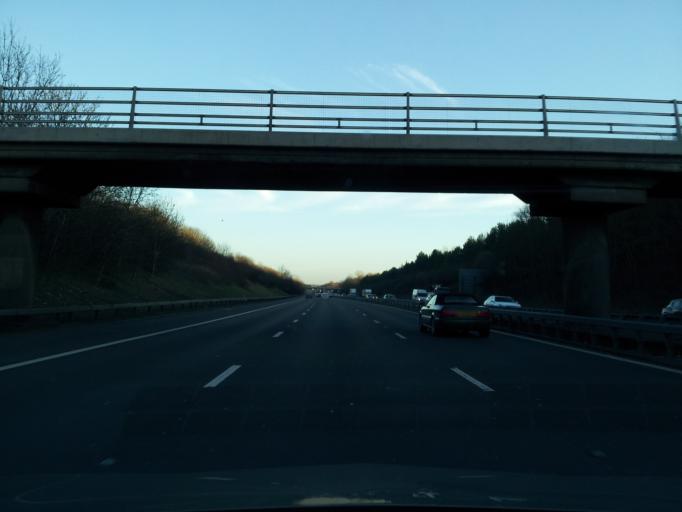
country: GB
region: England
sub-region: Milton Keynes
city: Newport Pagnell
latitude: 52.0768
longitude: -0.7371
